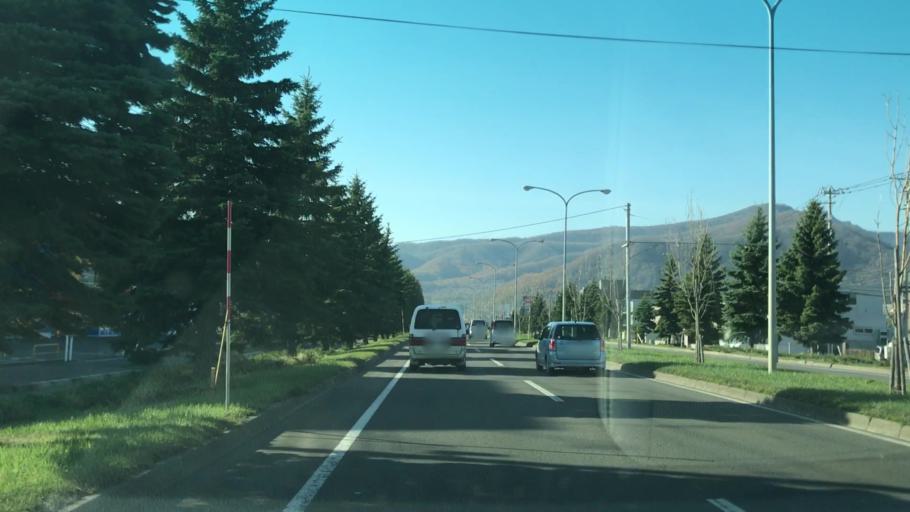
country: JP
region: Hokkaido
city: Sapporo
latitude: 43.1084
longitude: 141.2771
